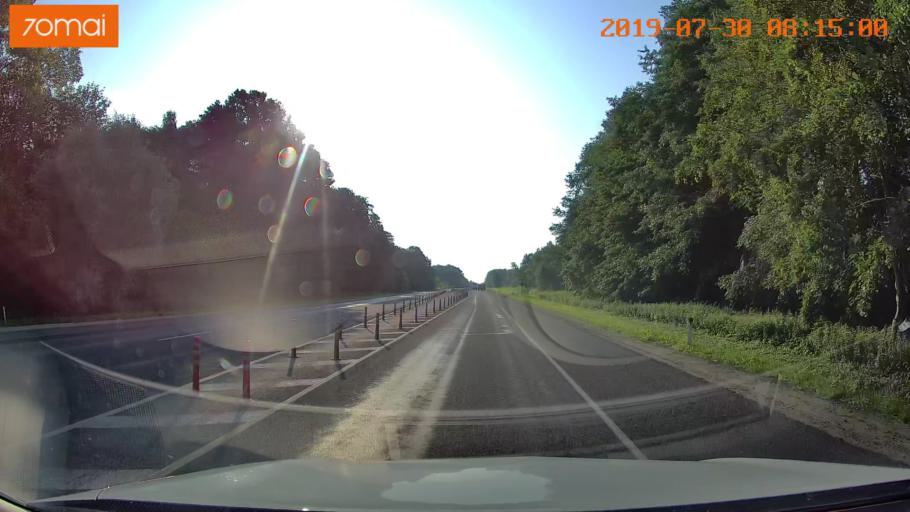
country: RU
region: Kaliningrad
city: Zheleznodorozhnyy
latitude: 54.6460
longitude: 21.3728
